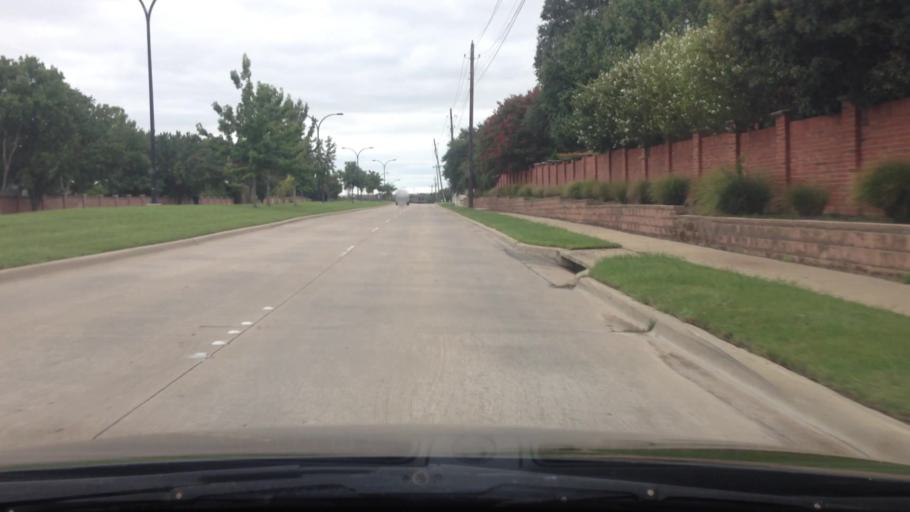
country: US
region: Texas
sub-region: Tarrant County
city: Keller
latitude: 32.9053
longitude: -97.2355
